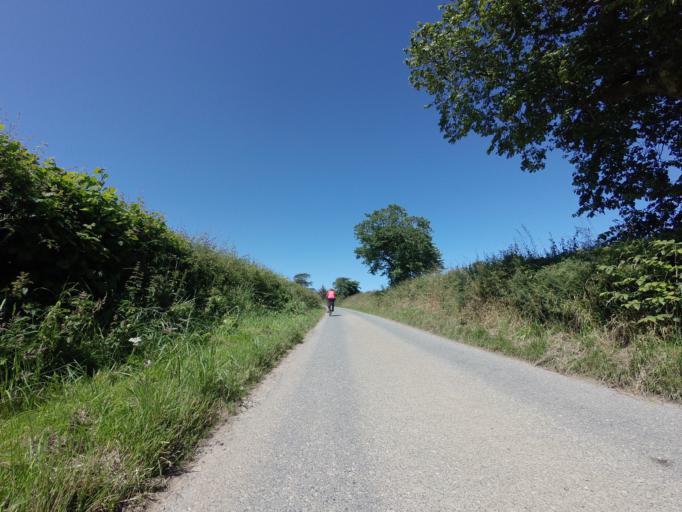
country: GB
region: Scotland
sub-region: Aberdeenshire
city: Macduff
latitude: 57.6366
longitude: -2.4920
